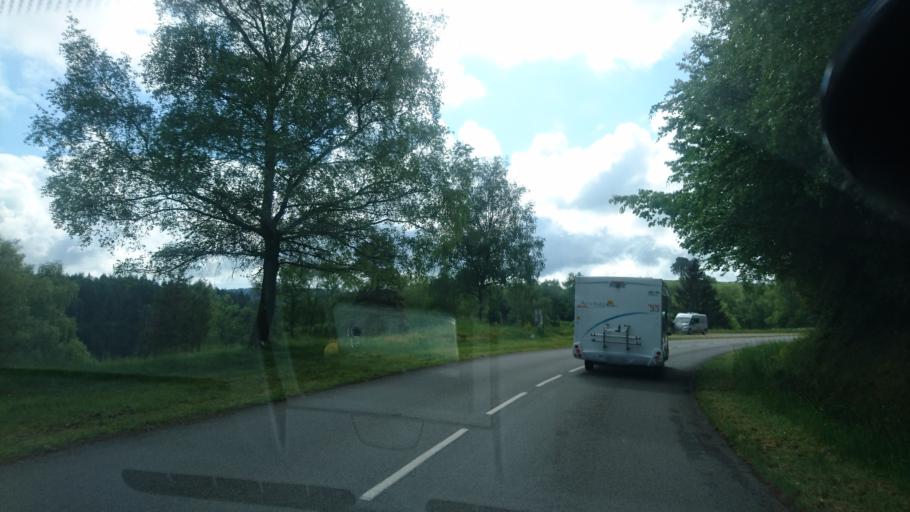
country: FR
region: Limousin
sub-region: Departement de la Haute-Vienne
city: Peyrat-le-Chateau
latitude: 45.7809
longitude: 1.8492
